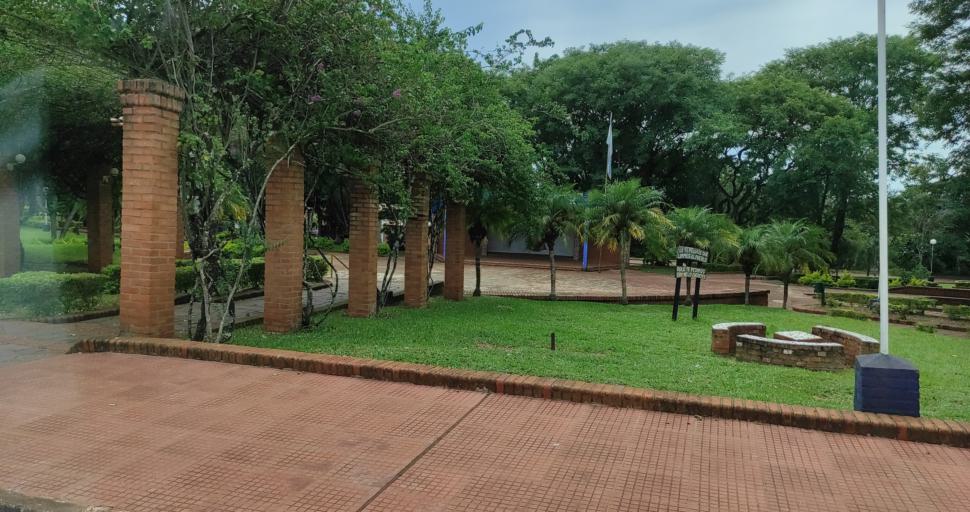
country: AR
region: Misiones
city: El Alcazar
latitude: -26.7167
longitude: -54.8137
